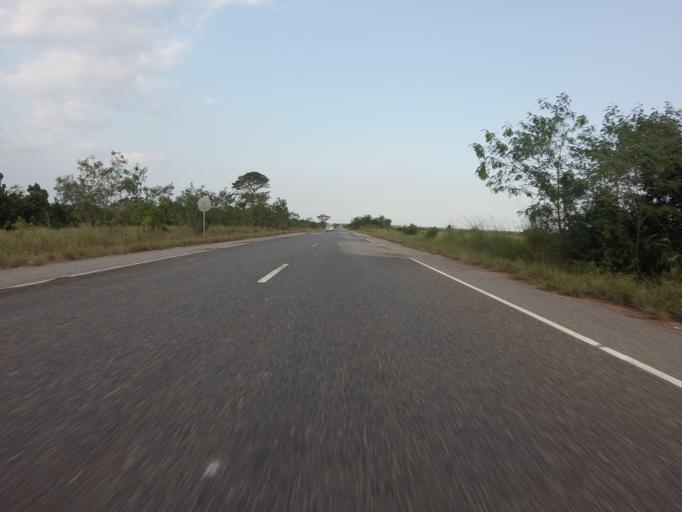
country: GH
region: Volta
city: Anloga
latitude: 6.0844
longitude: 0.5582
